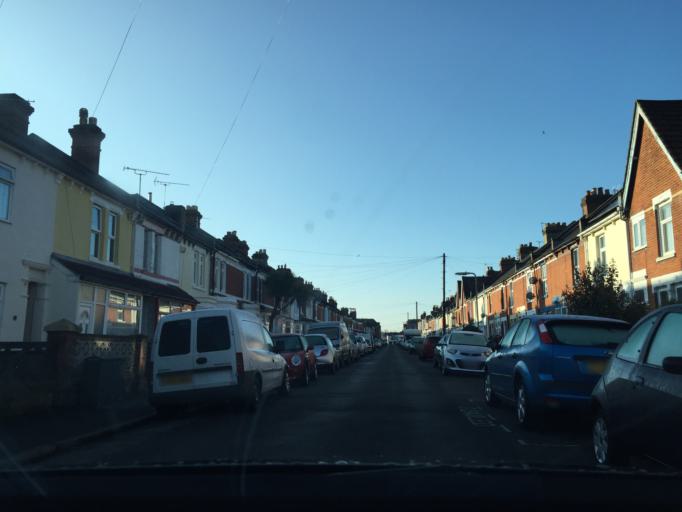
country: GB
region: England
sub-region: Hampshire
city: Gosport
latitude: 50.8020
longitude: -1.1333
